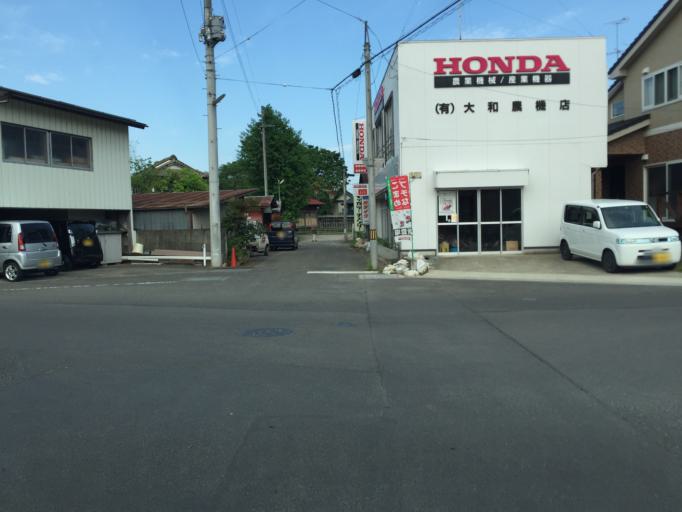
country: JP
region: Fukushima
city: Yanagawamachi-saiwaicho
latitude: 37.8601
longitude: 140.6072
